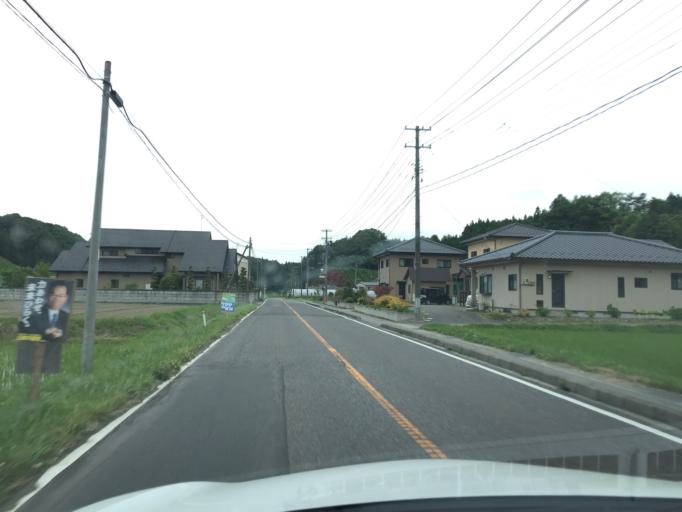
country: JP
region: Fukushima
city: Funehikimachi-funehiki
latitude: 37.3131
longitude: 140.6584
